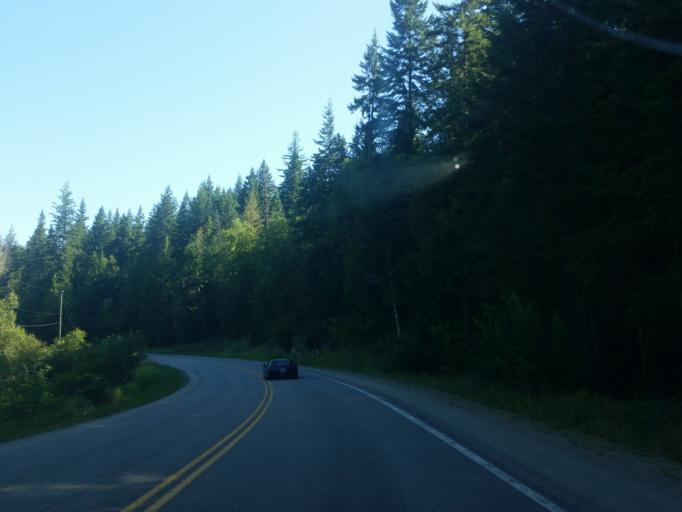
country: CA
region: British Columbia
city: Sicamous
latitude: 50.7258
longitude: -119.0312
